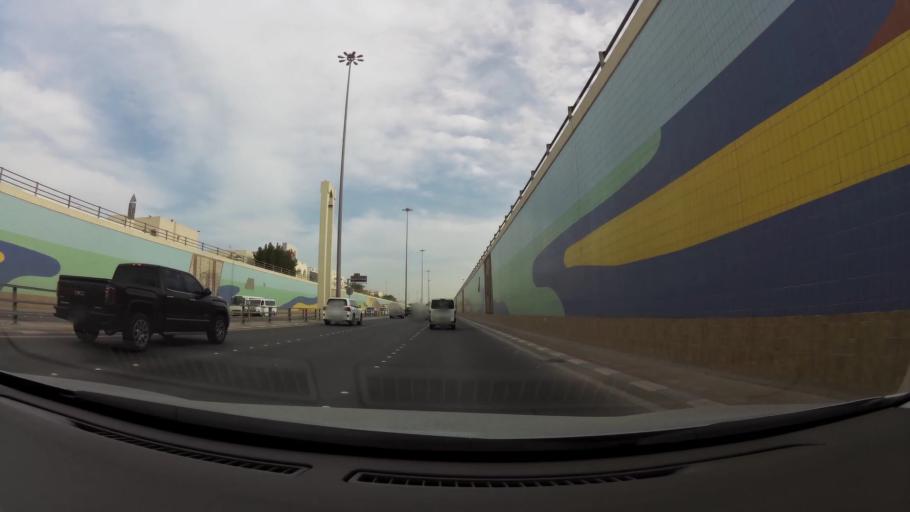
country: QA
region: Baladiyat ad Dawhah
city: Doha
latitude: 25.2630
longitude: 51.4977
